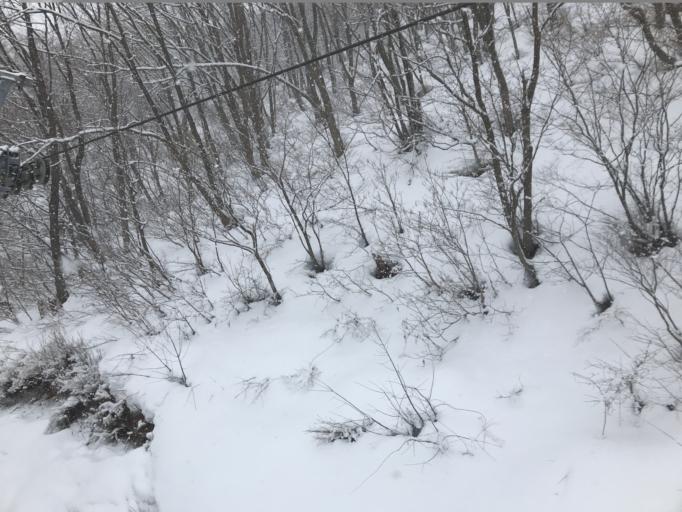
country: JP
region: Nagano
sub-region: Kitaazumi Gun
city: Hakuba
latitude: 36.7547
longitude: 137.8545
